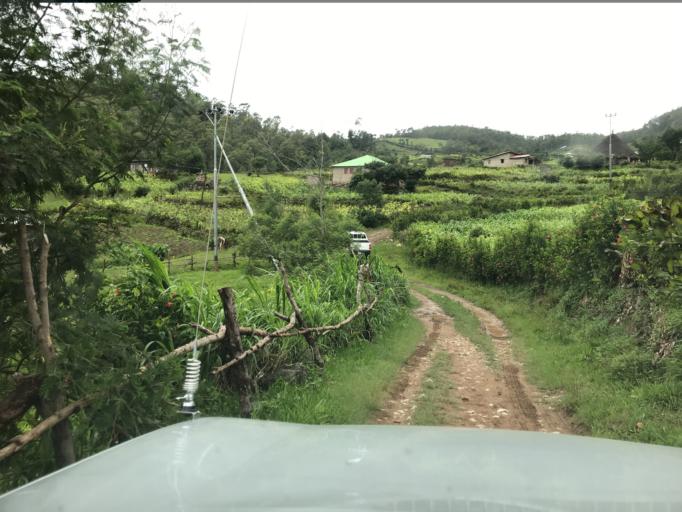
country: TL
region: Ainaro
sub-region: Ainaro
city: Ainaro
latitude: -8.8686
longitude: 125.5522
